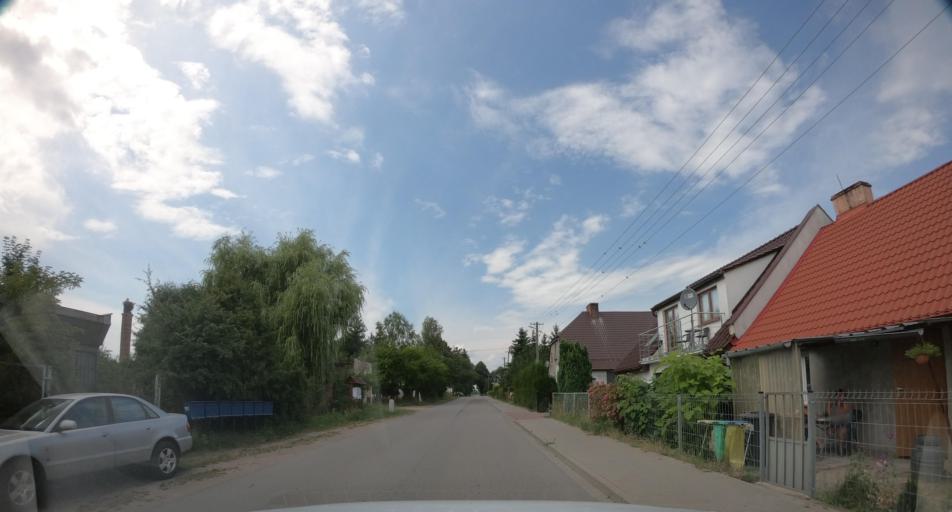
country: PL
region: West Pomeranian Voivodeship
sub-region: Powiat walecki
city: Tuczno
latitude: 53.2338
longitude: 16.1609
